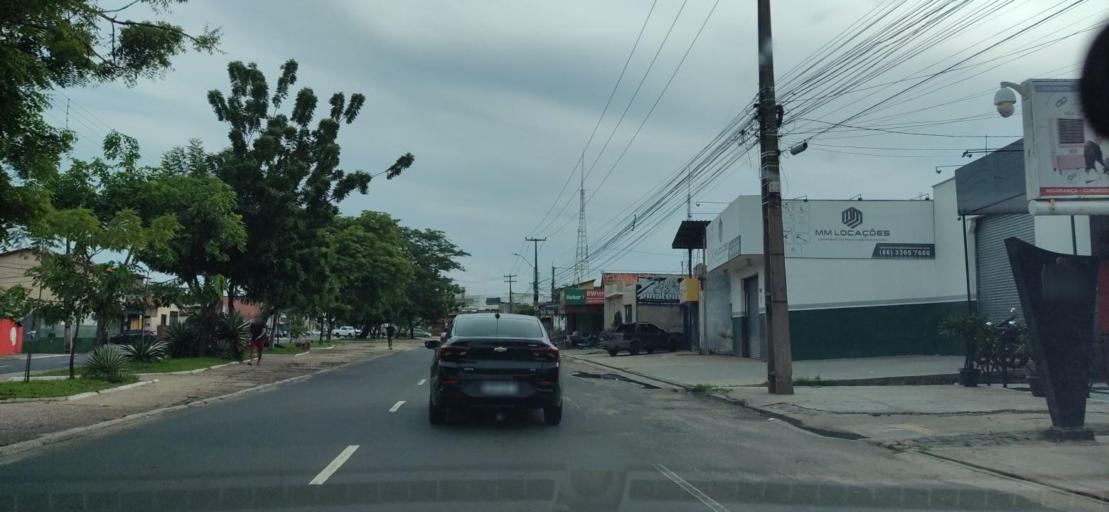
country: BR
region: Piaui
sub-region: Teresina
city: Teresina
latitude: -5.1082
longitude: -42.7928
